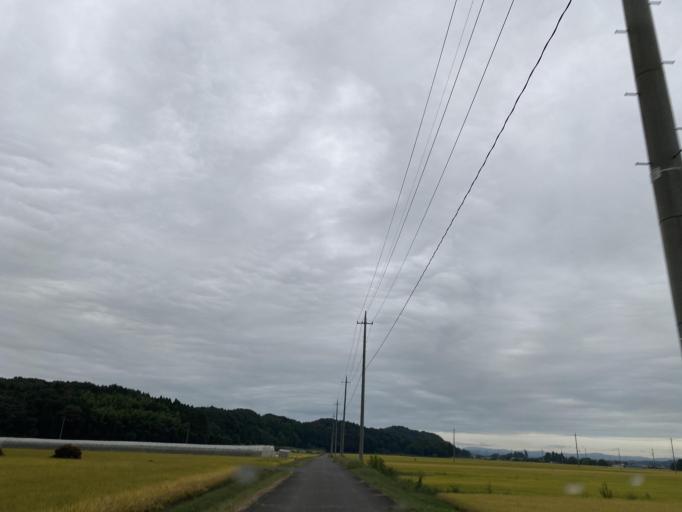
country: JP
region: Fukushima
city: Sukagawa
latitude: 37.2879
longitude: 140.2482
